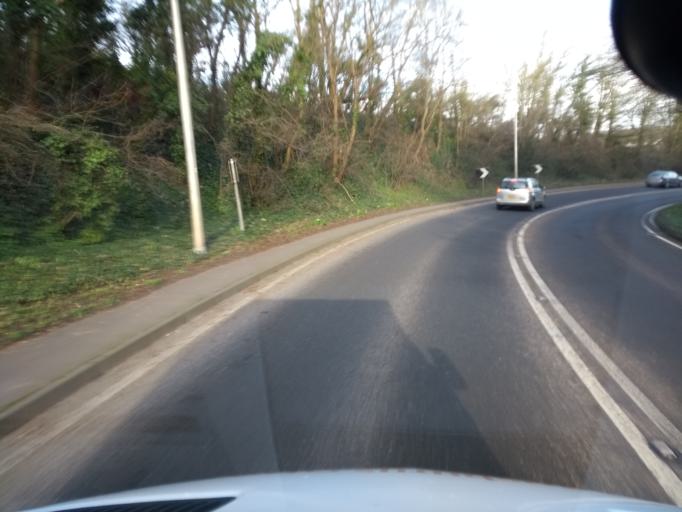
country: GB
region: England
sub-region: North Somerset
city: Bleadon
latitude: 51.3191
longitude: -2.9703
